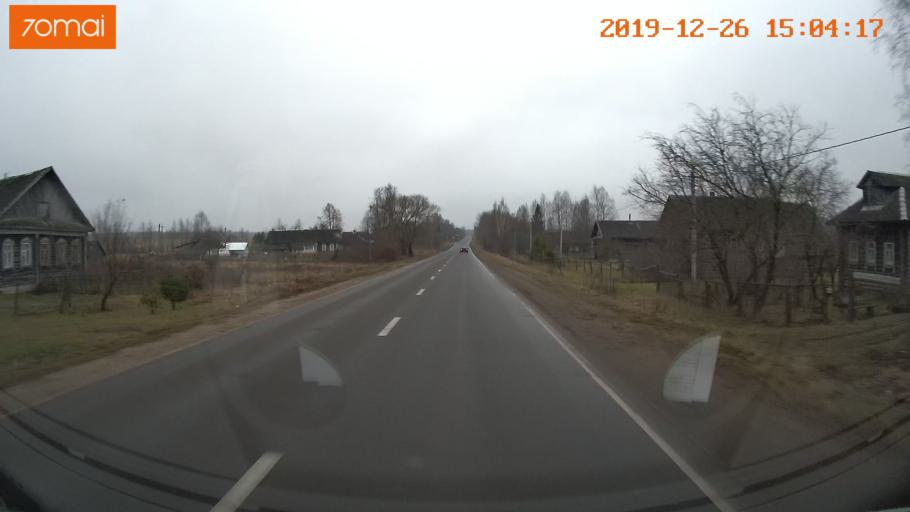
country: RU
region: Jaroslavl
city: Rybinsk
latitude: 58.2018
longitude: 38.8636
